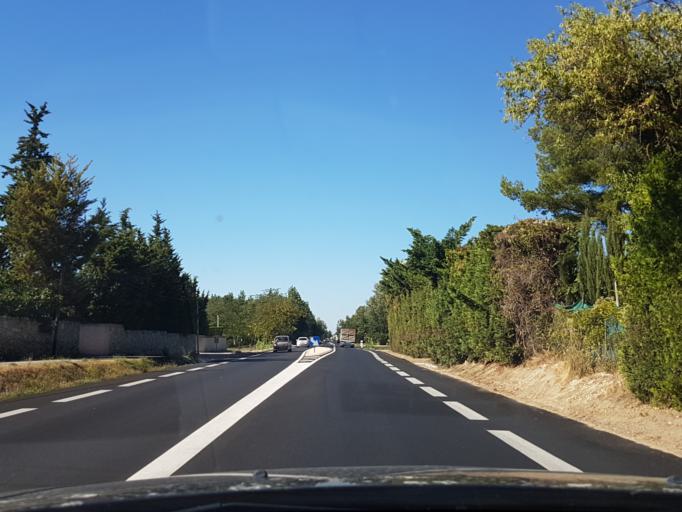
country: FR
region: Provence-Alpes-Cote d'Azur
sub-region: Departement du Vaucluse
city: Velleron
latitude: 43.9343
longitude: 5.0301
